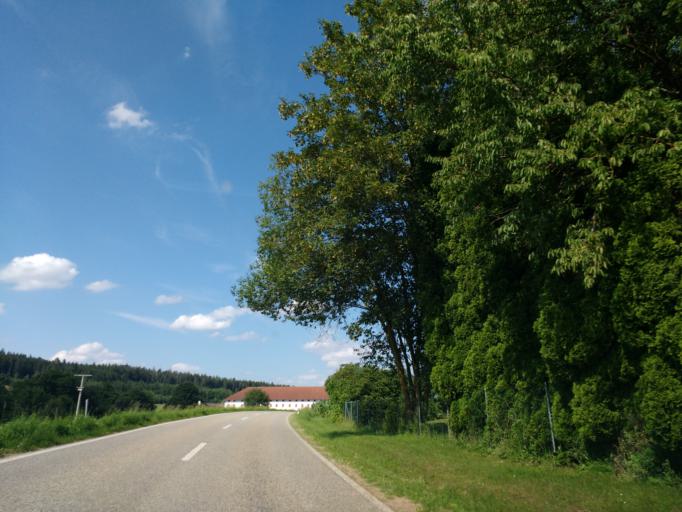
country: DE
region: Bavaria
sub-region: Upper Bavaria
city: Taufkirchen
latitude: 48.1262
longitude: 12.4240
